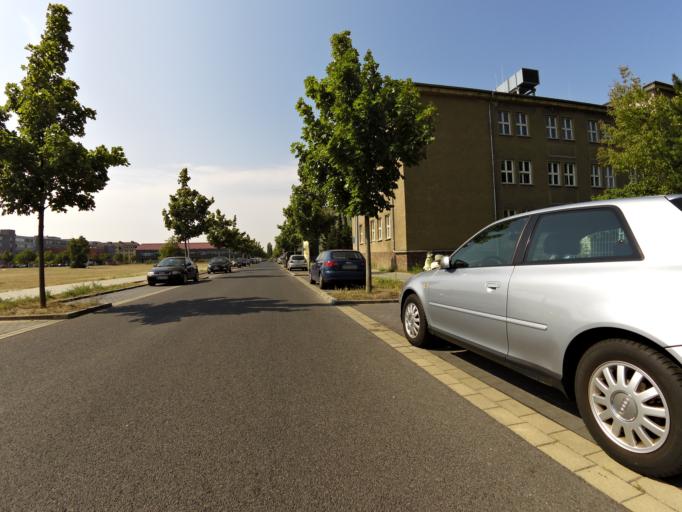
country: DE
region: Berlin
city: Adlershof
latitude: 52.4355
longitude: 13.5361
